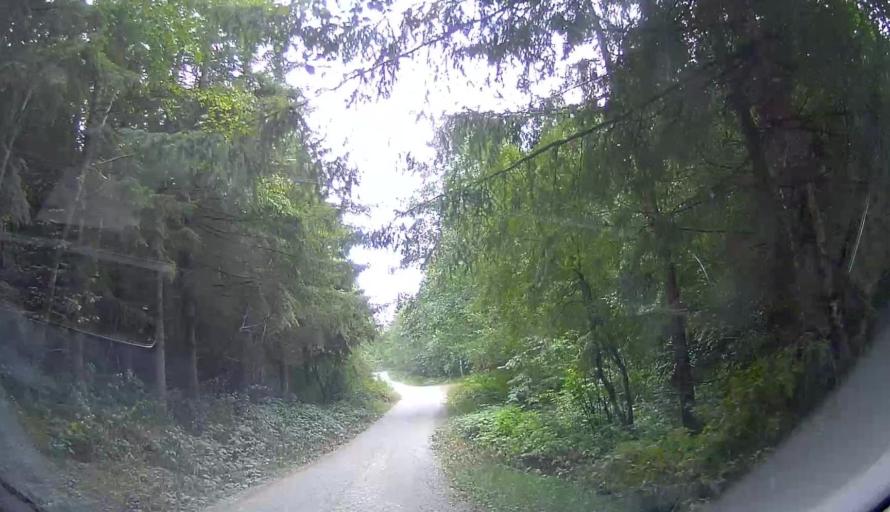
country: US
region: Washington
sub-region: Whatcom County
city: Sudden Valley
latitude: 48.6126
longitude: -122.4178
